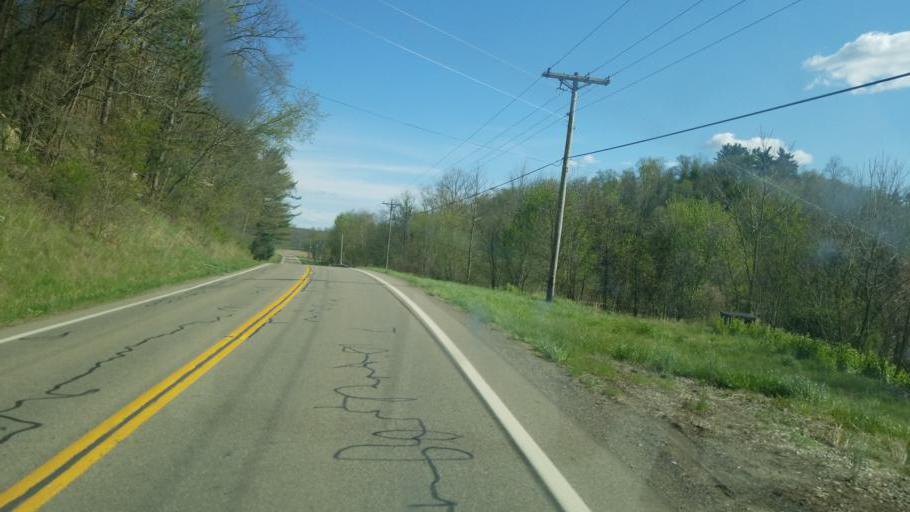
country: US
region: Ohio
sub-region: Coshocton County
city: Coshocton
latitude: 40.3415
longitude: -81.8821
